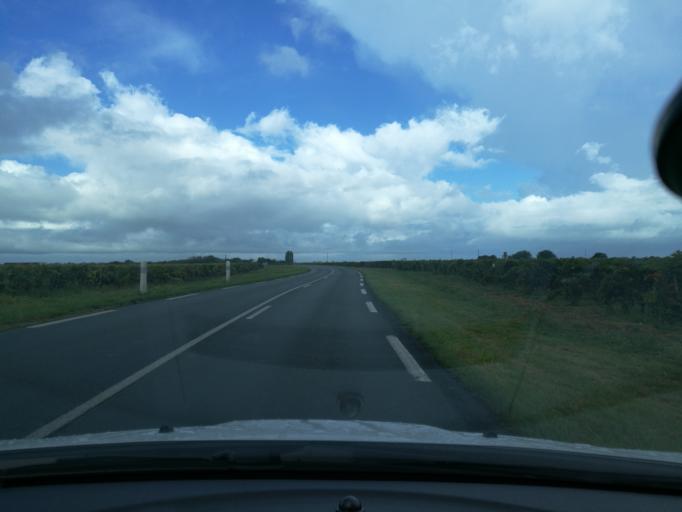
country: FR
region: Poitou-Charentes
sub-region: Departement de la Charente-Maritime
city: Le Bois-Plage-en-Re
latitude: 46.1999
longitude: -1.3907
